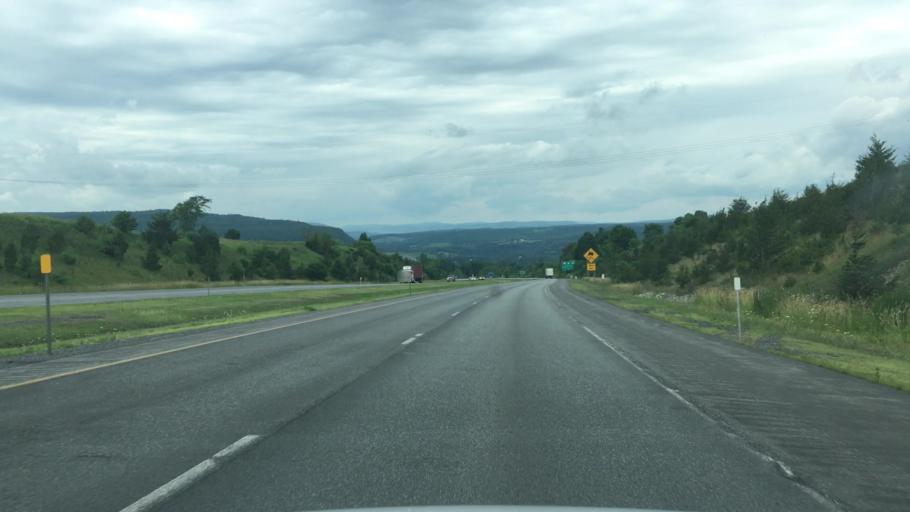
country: US
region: New York
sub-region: Schoharie County
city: Schoharie
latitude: 42.7122
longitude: -74.2849
